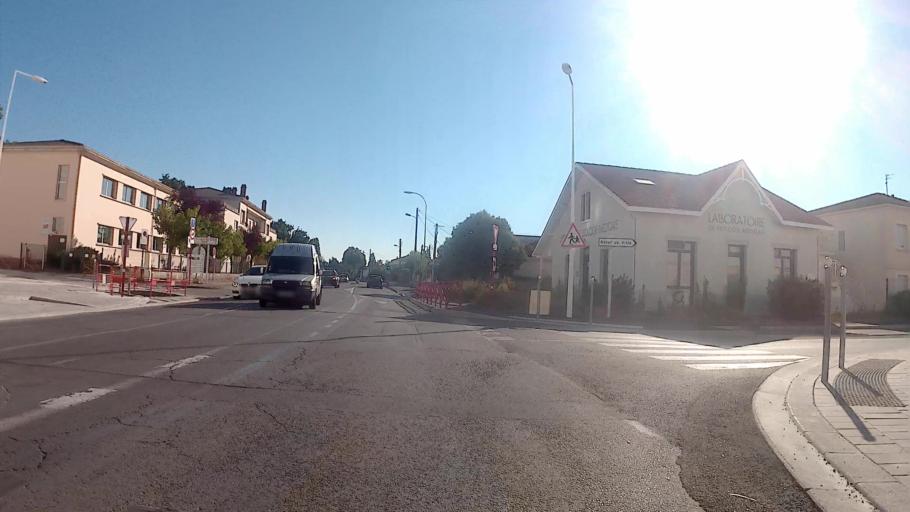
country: FR
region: Aquitaine
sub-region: Departement de la Gironde
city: Villenave-d'Ornon
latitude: 44.7820
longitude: -0.5679
